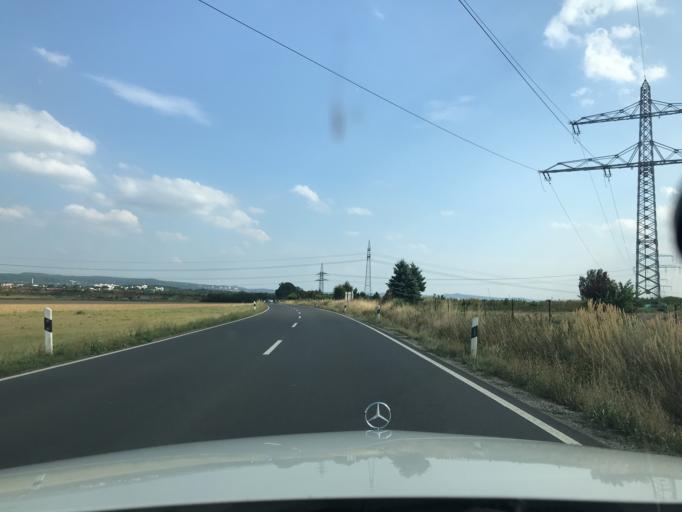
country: DE
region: Lower Saxony
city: Bovenden
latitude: 51.5721
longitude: 9.8788
